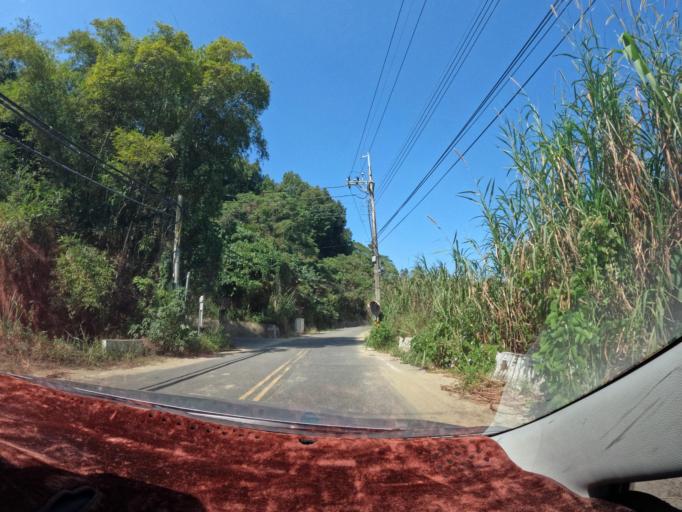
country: TW
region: Taiwan
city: Yujing
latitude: 23.0530
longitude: 120.3786
